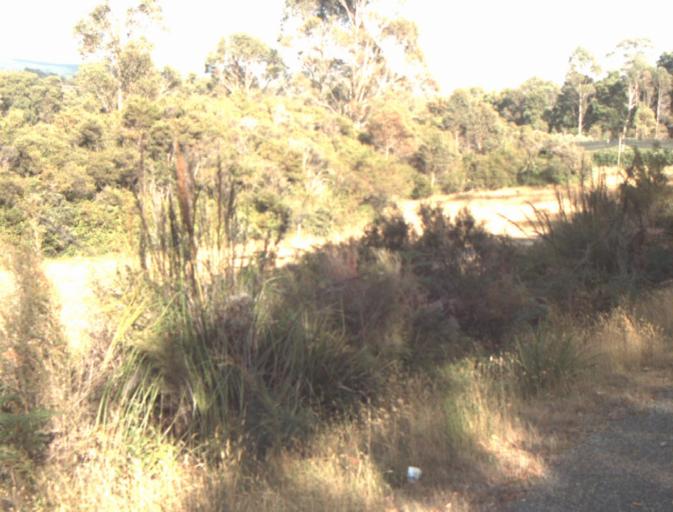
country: AU
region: Tasmania
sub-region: Dorset
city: Bridport
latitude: -41.1468
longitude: 147.2323
